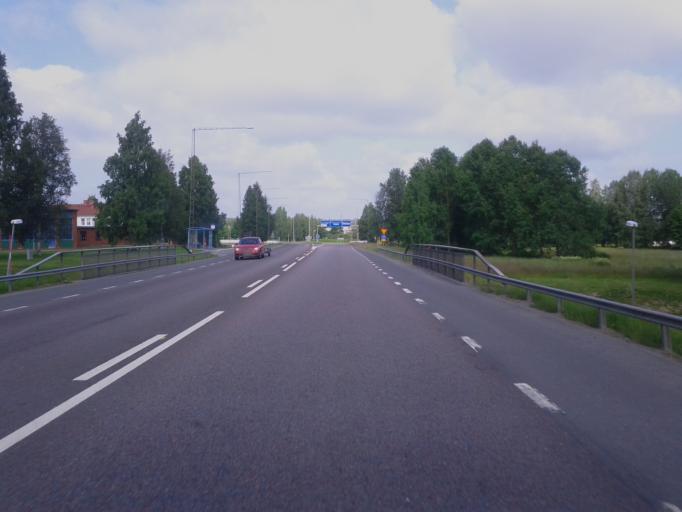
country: SE
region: Vaesterbotten
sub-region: Skelleftea Kommun
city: Skelleftea
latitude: 64.7410
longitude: 20.9629
